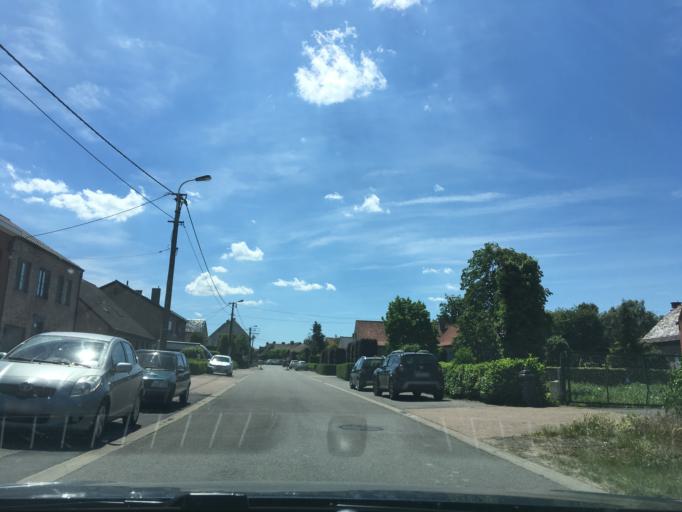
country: BE
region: Flanders
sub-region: Provincie West-Vlaanderen
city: Lichtervelde
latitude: 51.0327
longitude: 3.1298
